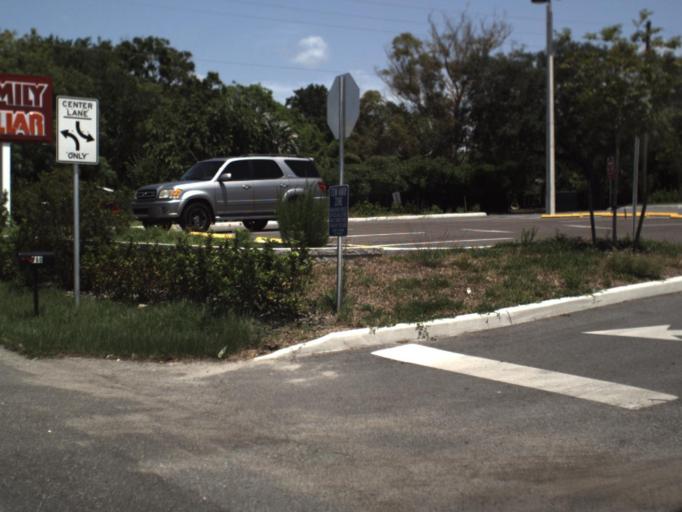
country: US
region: Florida
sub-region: Pinellas County
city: Palm Harbor
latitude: 28.0749
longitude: -82.7672
